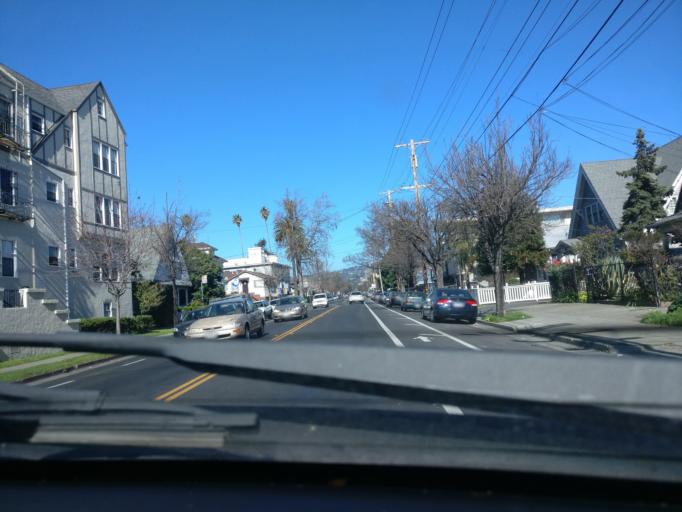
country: US
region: California
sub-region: Alameda County
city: Alameda
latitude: 37.7857
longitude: -122.2220
